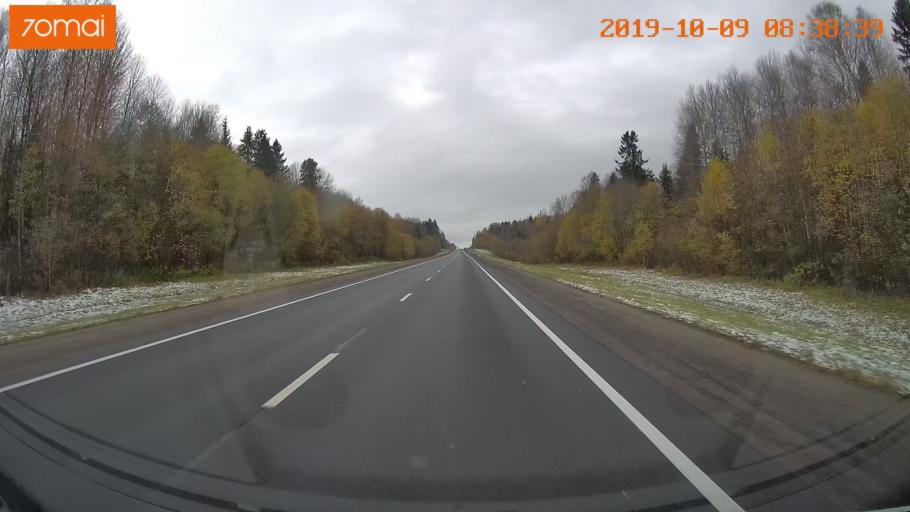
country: RU
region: Vologda
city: Gryazovets
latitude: 58.9596
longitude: 40.1631
